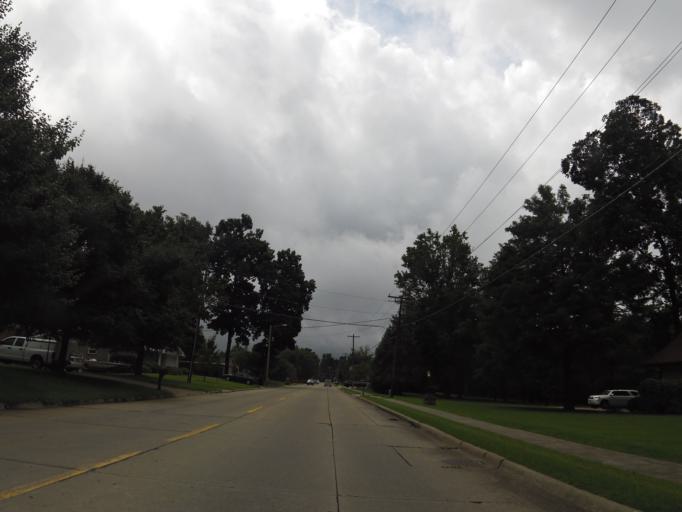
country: US
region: Missouri
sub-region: Cape Girardeau County
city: Cape Girardeau
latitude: 37.3410
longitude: -89.5549
